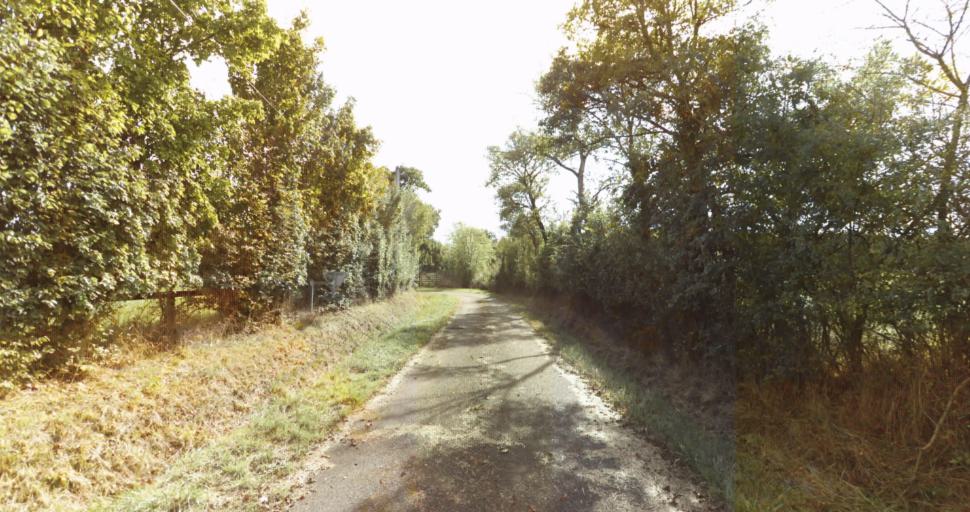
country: FR
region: Lower Normandy
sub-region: Departement de l'Orne
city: Sees
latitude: 48.6974
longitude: 0.1960
